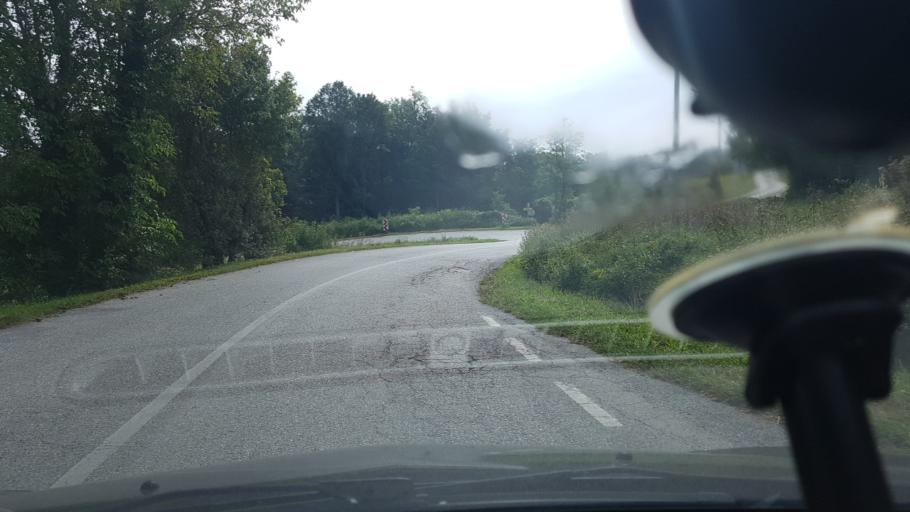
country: HR
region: Varazdinska
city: Ljubescica
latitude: 46.0960
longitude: 16.3396
